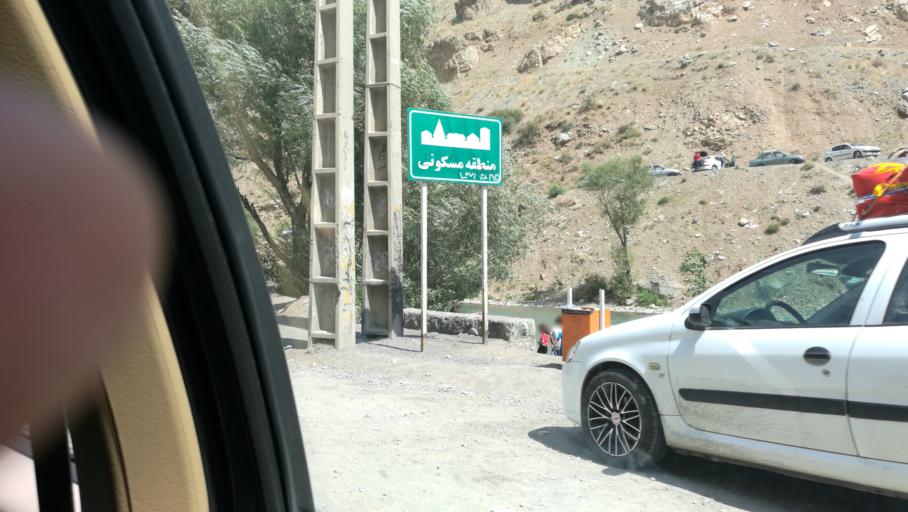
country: IR
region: Alborz
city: Karaj
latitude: 36.0154
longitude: 51.1453
